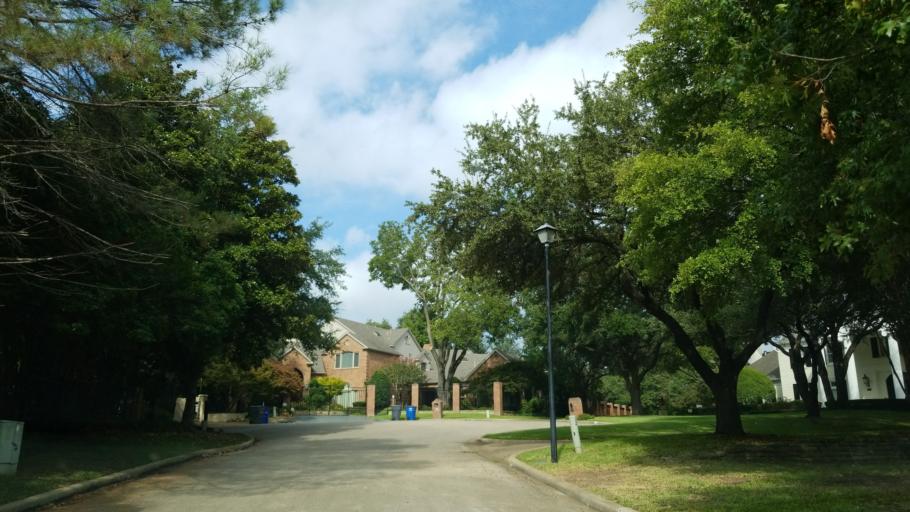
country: US
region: Texas
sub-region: Dallas County
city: Addison
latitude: 32.9420
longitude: -96.8002
